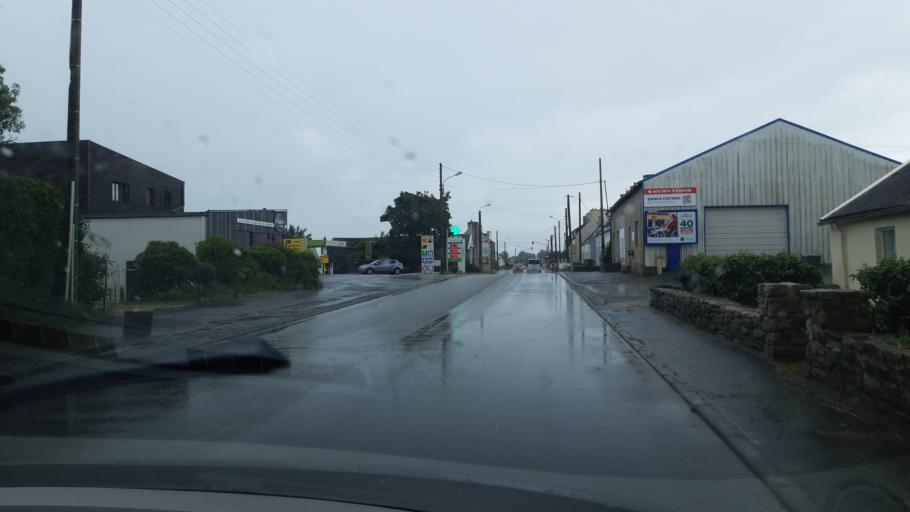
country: FR
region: Brittany
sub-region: Departement du Finistere
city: Plouvorn
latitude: 48.5799
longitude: -4.0483
